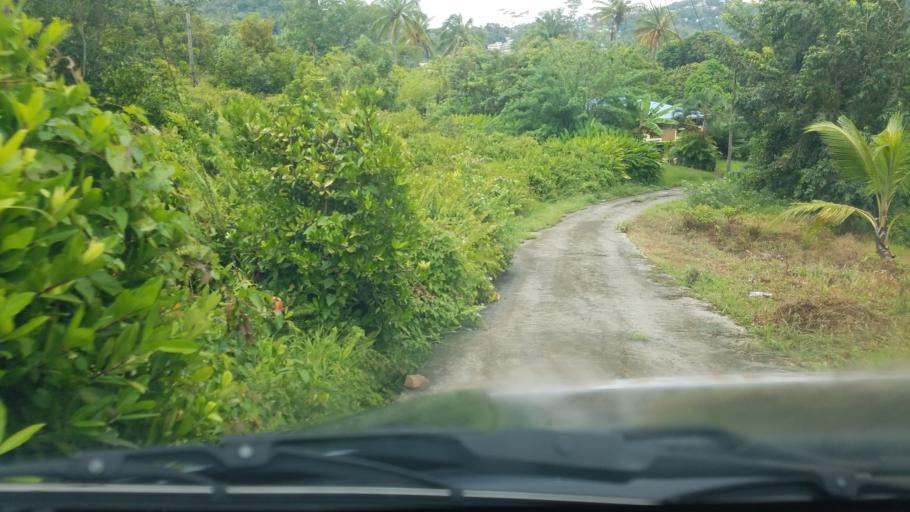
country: LC
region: Castries Quarter
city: Bisee
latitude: 13.9935
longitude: -60.9582
